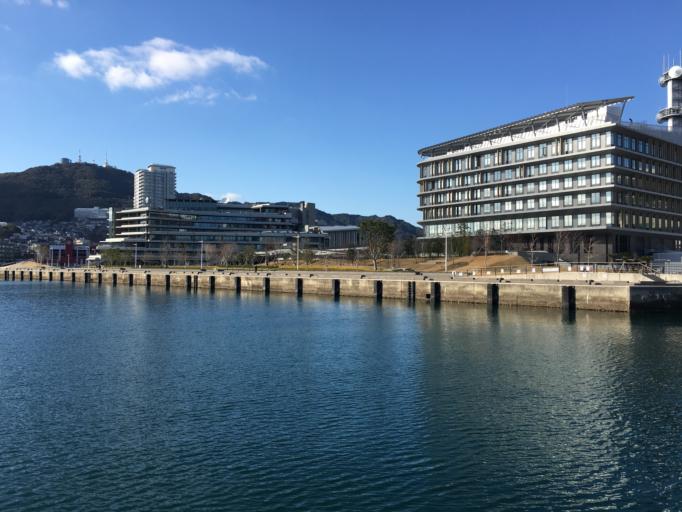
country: JP
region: Nagasaki
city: Nagasaki-shi
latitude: 32.7485
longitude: 129.8707
